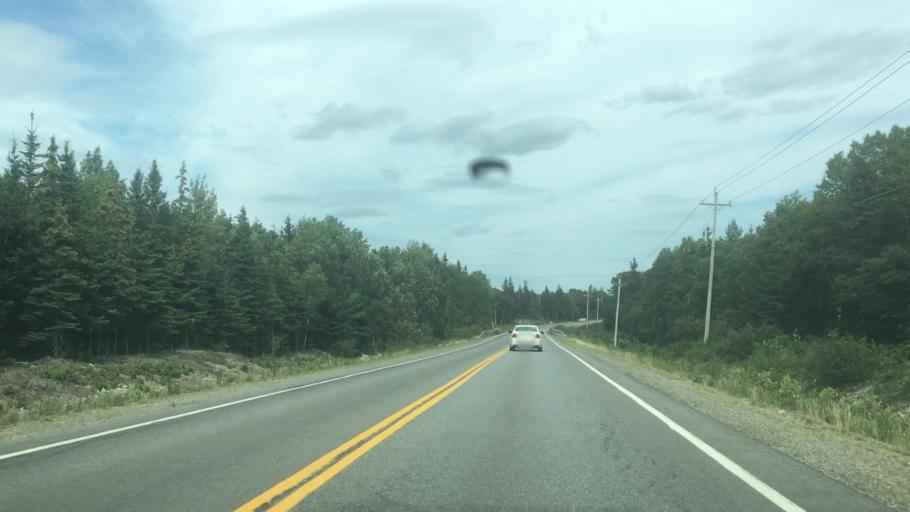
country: CA
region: Nova Scotia
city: Sydney Mines
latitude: 46.5121
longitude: -60.4304
